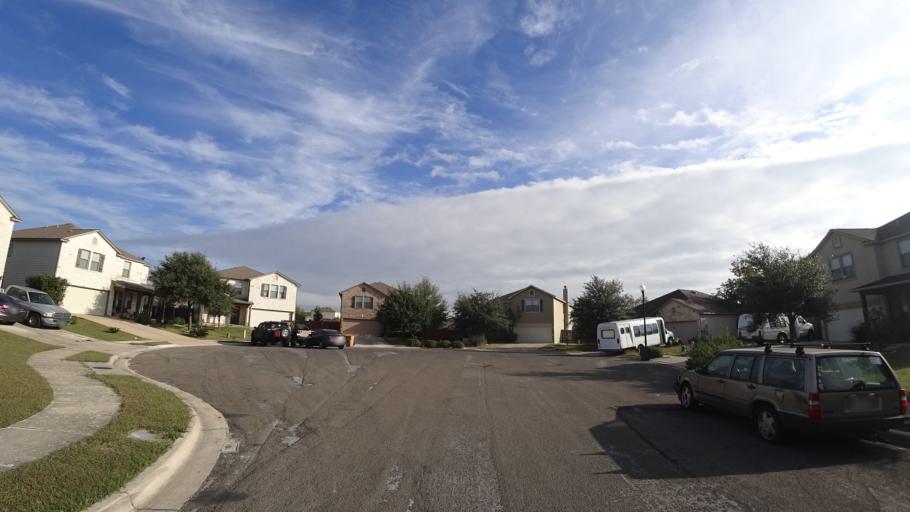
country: US
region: Texas
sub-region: Travis County
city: Austin
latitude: 30.1968
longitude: -97.7281
